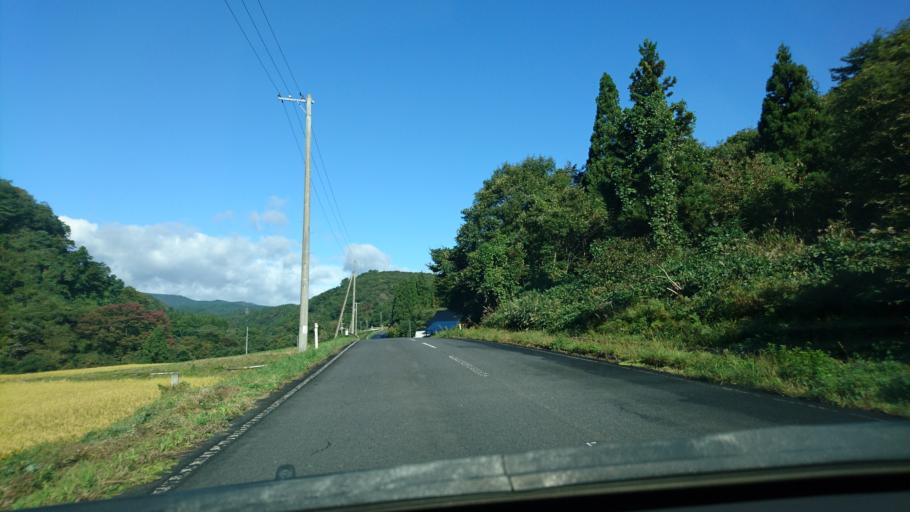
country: JP
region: Iwate
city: Ichinoseki
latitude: 39.0212
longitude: 141.0216
